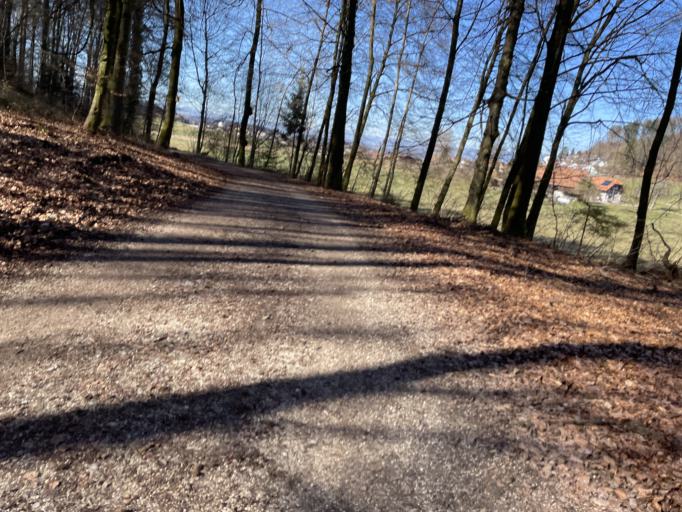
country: CH
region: Bern
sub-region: Bern-Mittelland District
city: Bariswil
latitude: 47.0133
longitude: 7.5331
